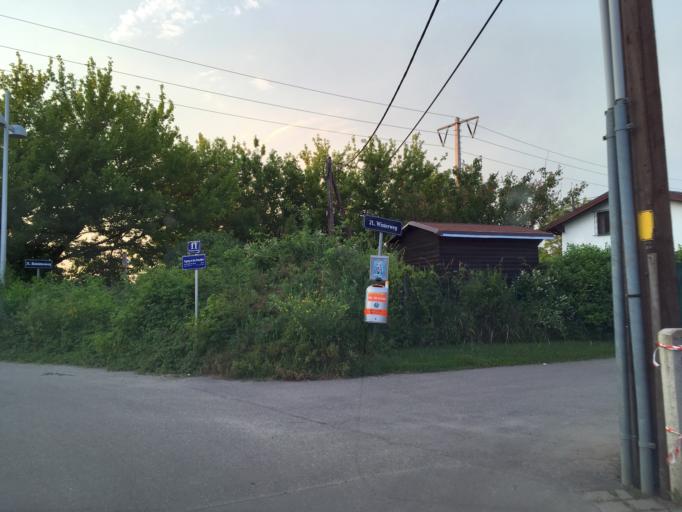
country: AT
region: Lower Austria
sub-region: Politischer Bezirk Wien-Umgebung
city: Gerasdorf bei Wien
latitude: 48.2798
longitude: 16.4618
